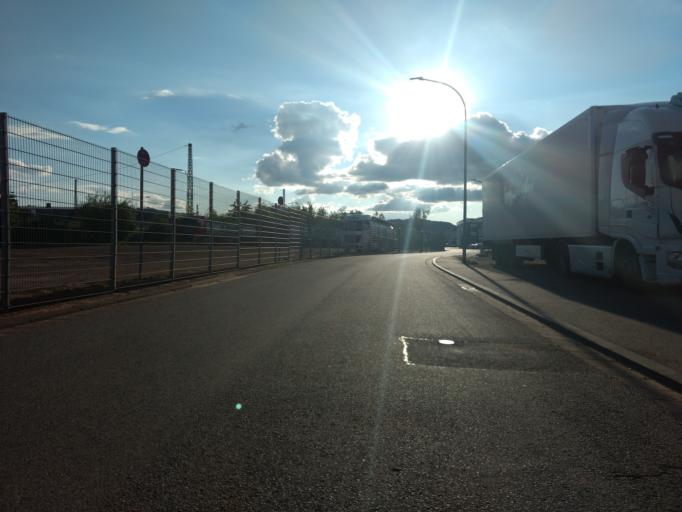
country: DE
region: Saarland
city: Saarlouis
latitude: 49.3268
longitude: 6.7584
